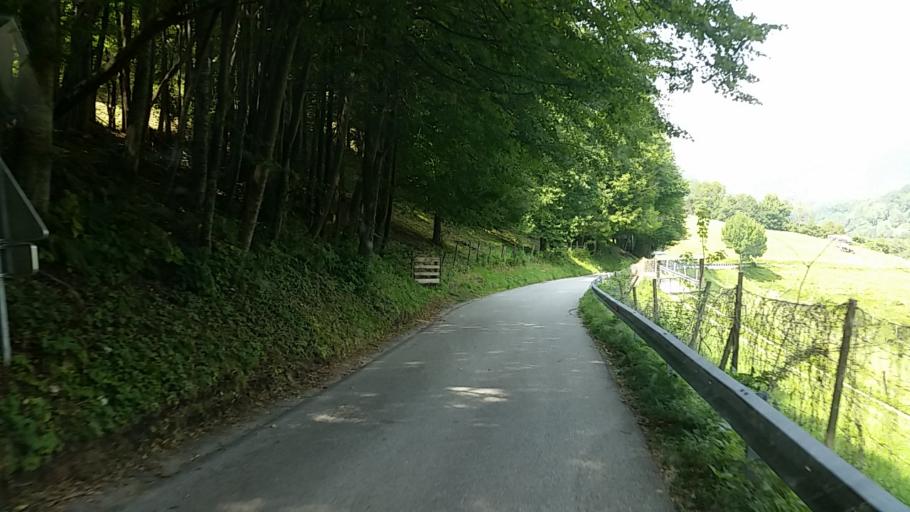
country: SI
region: Tolmin
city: Tolmin
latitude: 46.1397
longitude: 13.7703
